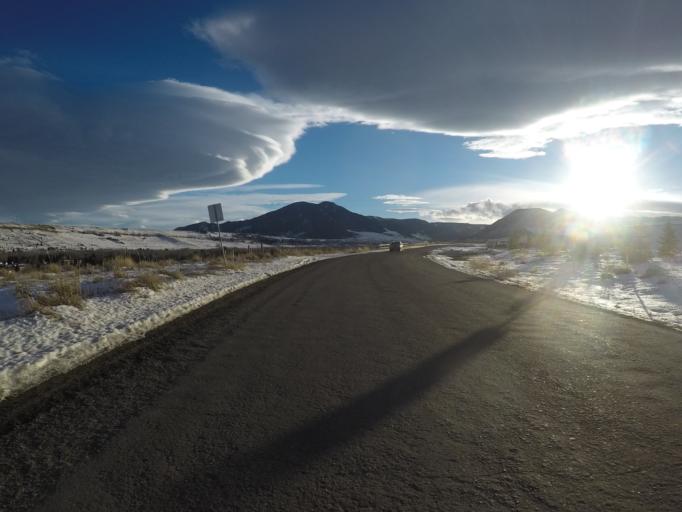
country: US
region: Montana
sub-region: Carbon County
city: Red Lodge
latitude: 45.1862
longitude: -109.2529
